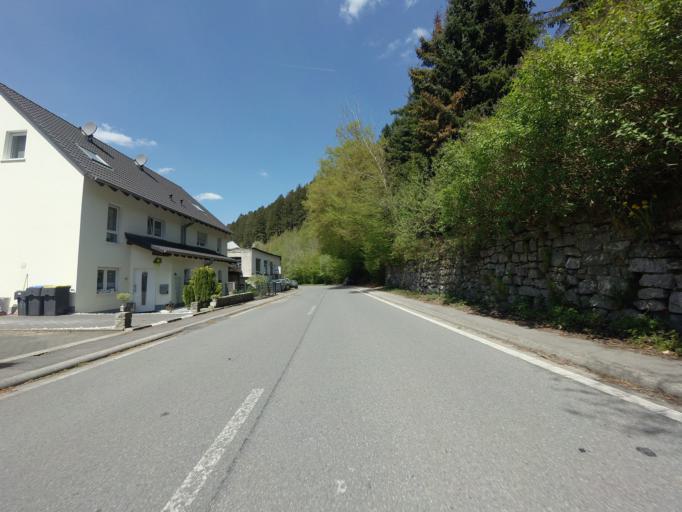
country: DE
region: North Rhine-Westphalia
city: Hemer
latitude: 51.3514
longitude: 7.7940
